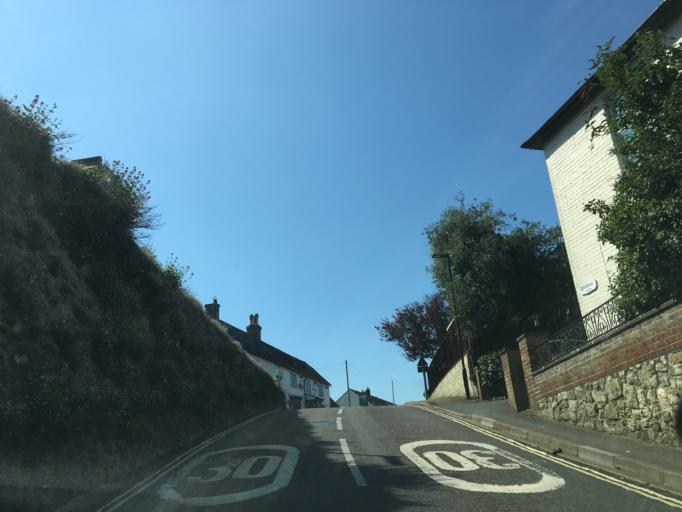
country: GB
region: England
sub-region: Isle of Wight
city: Newchurch
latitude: 50.6670
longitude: -1.2067
